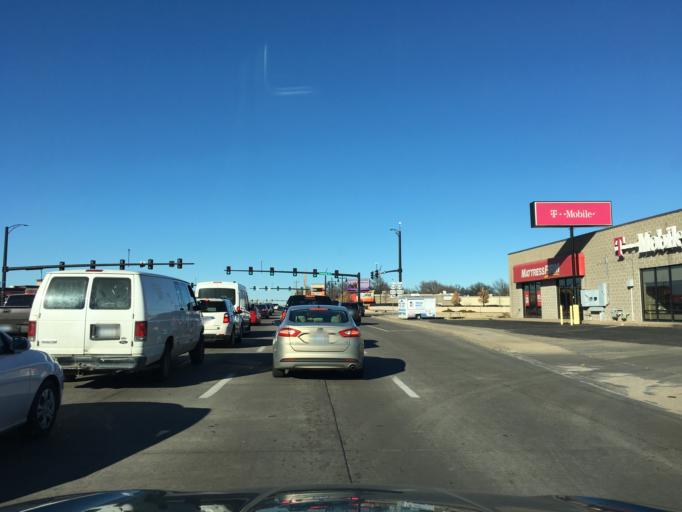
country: US
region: Kansas
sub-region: Sedgwick County
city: Bellaire
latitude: 37.6783
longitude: -97.2443
